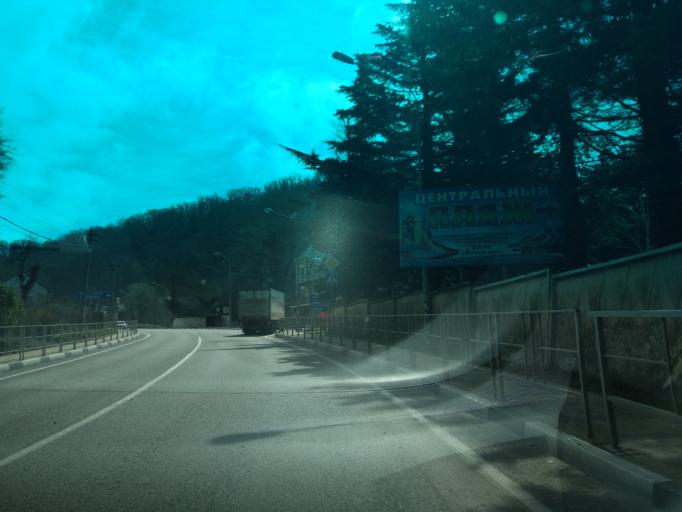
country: RU
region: Krasnodarskiy
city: Shepsi
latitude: 44.0373
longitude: 39.1503
